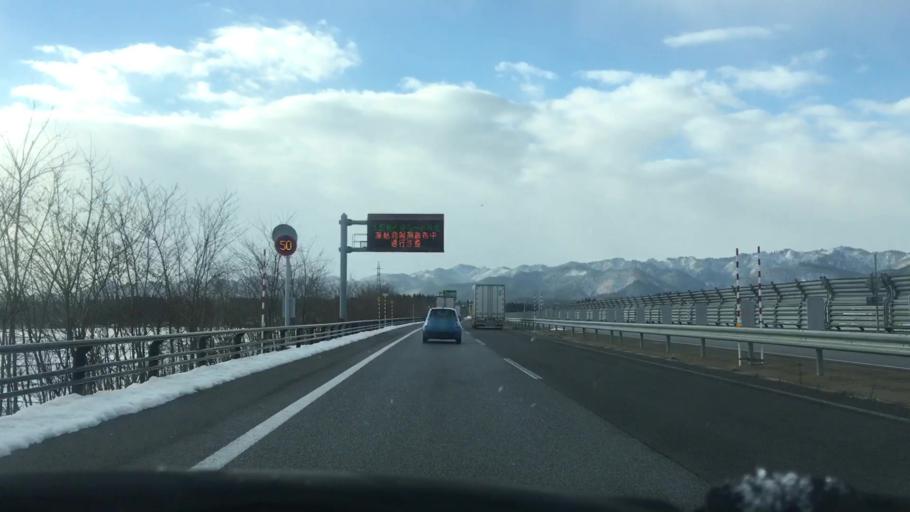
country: JP
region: Akita
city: Odate
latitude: 40.2554
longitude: 140.5201
